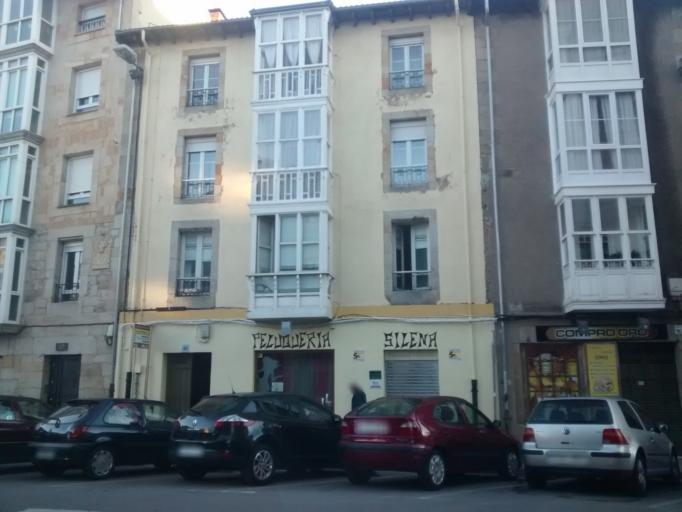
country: ES
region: Cantabria
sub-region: Provincia de Cantabria
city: Reinosa
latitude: 43.0018
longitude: -4.1363
